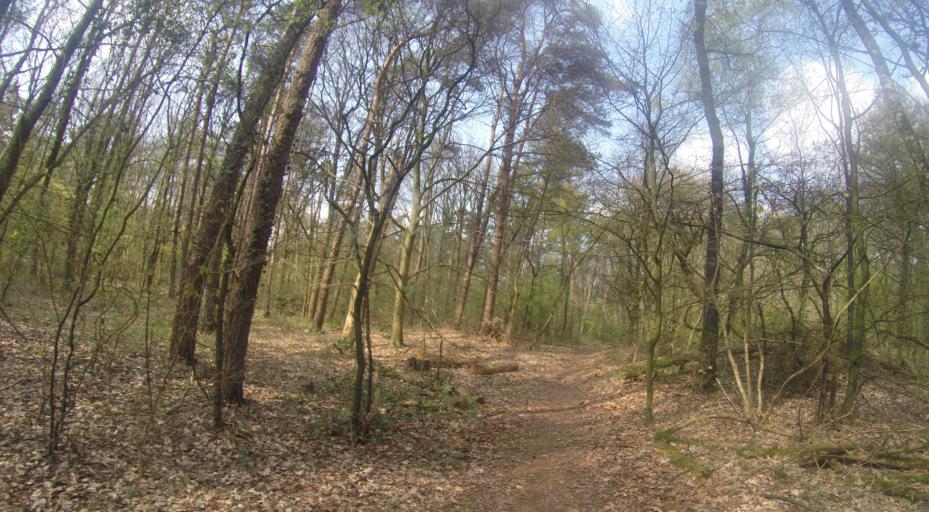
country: NL
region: Gelderland
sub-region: Gemeente Doetinchem
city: Doetinchem
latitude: 51.9500
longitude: 6.3251
